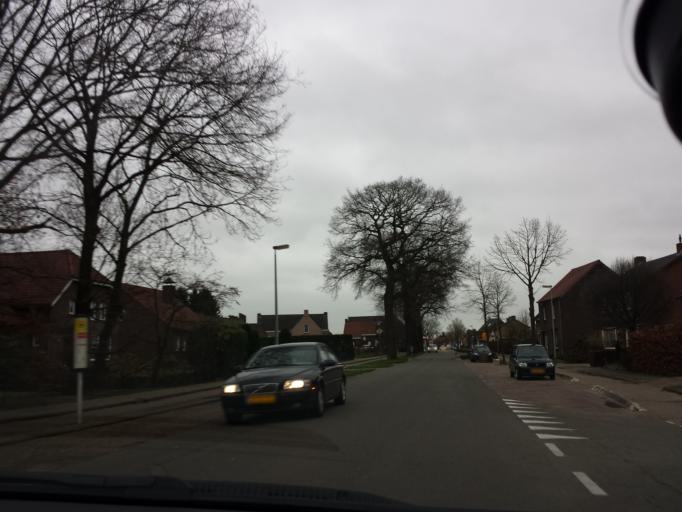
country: NL
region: Limburg
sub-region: Gemeente Roerdalen
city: Posterholt
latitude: 51.1295
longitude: 6.0205
